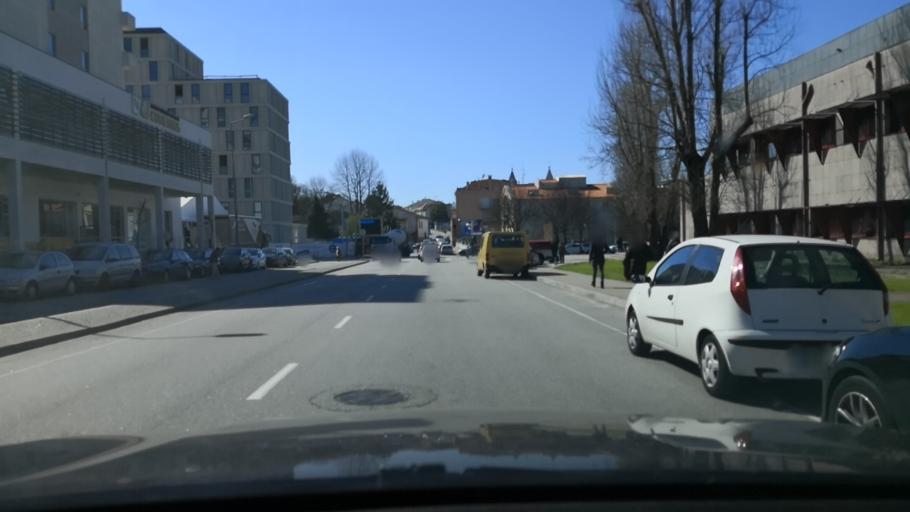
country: PT
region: Porto
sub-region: Porto
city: Porto
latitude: 41.1738
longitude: -8.6026
